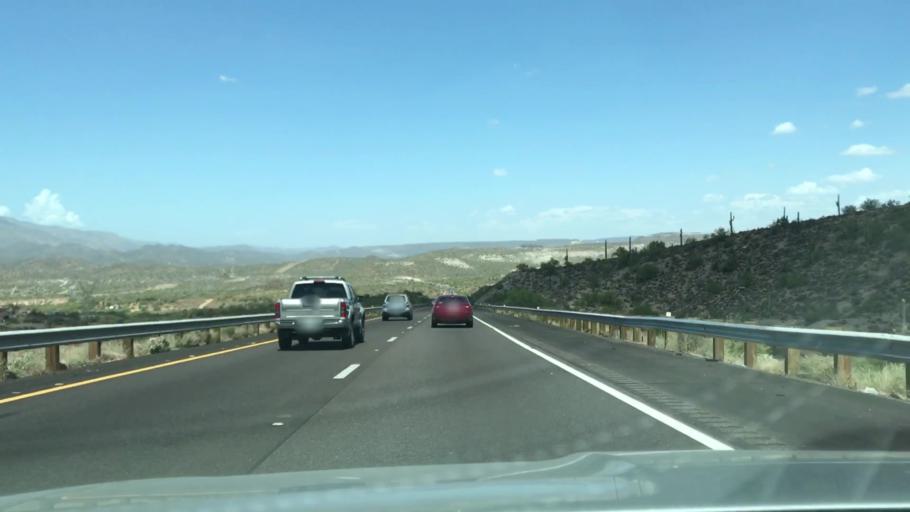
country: US
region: Arizona
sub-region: Maricopa County
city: New River
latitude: 33.9903
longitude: -112.1342
